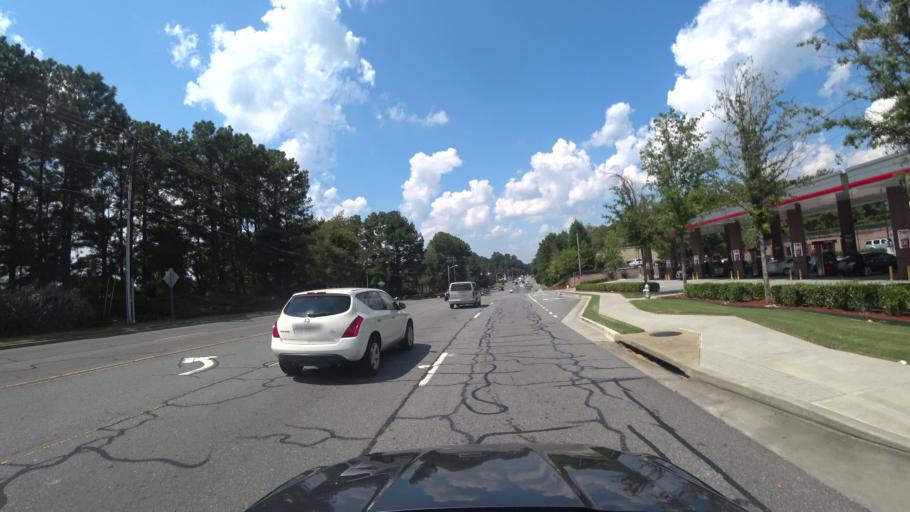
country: US
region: Georgia
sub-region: Gwinnett County
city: Norcross
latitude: 33.9413
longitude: -84.2496
